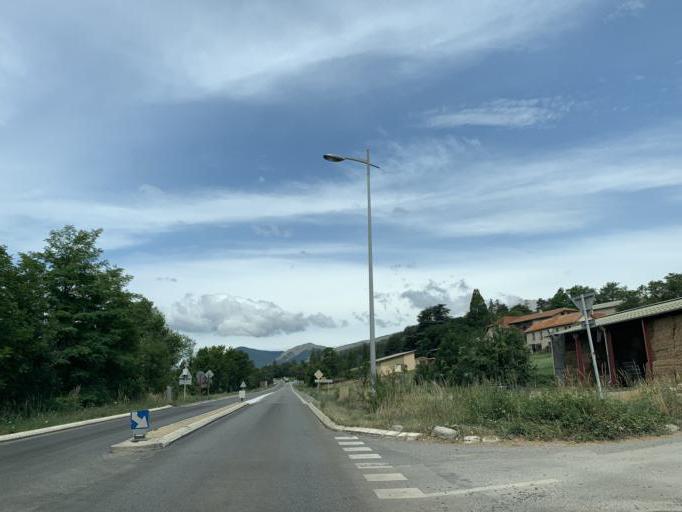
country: FR
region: Provence-Alpes-Cote d'Azur
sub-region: Departement des Hautes-Alpes
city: La Roche-des-Arnauds
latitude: 44.5422
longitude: 6.0117
